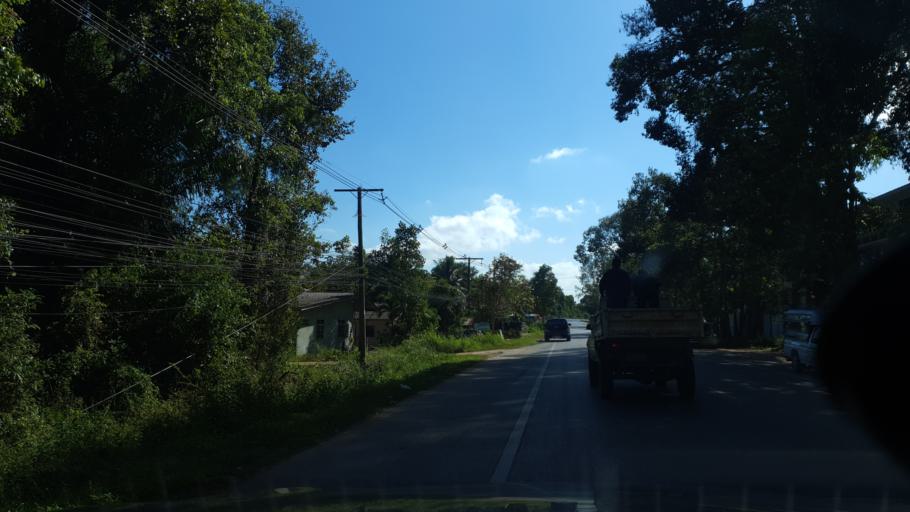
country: TH
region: Phangnga
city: Ban Ao Nang
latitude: 8.0298
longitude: 98.8661
